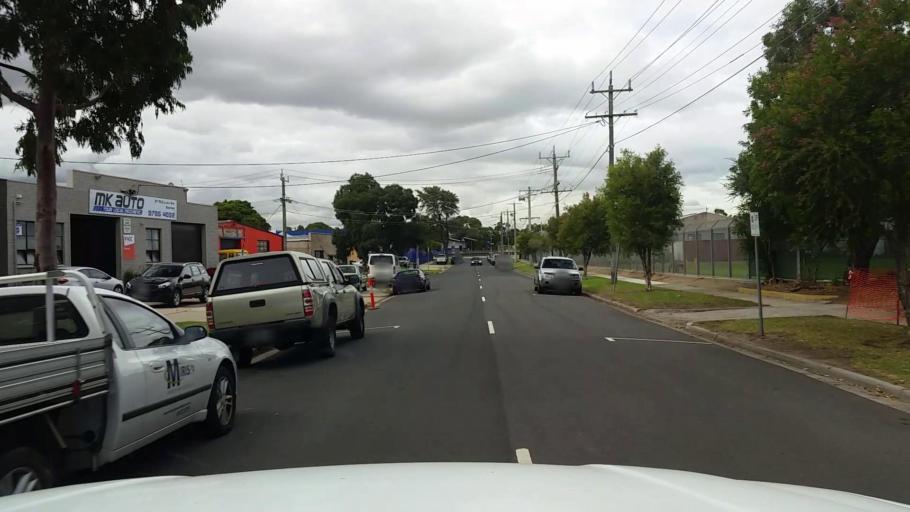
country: AU
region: Victoria
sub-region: Frankston
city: Frankston East
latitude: -38.1217
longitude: 145.1329
